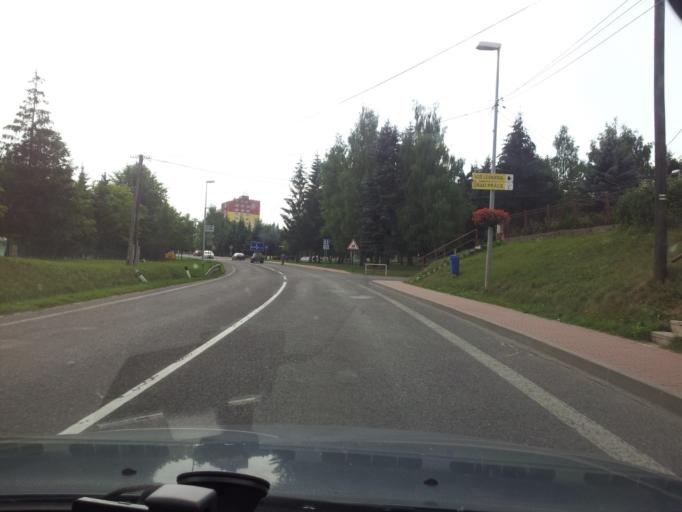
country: SK
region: Zilinsky
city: Tvrdosin
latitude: 49.3313
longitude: 19.5516
